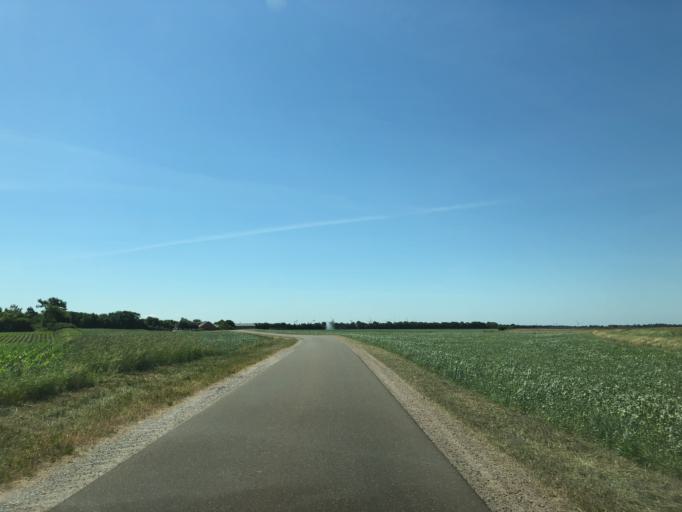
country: DK
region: Central Jutland
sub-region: Struer Kommune
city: Struer
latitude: 56.4170
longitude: 8.4264
